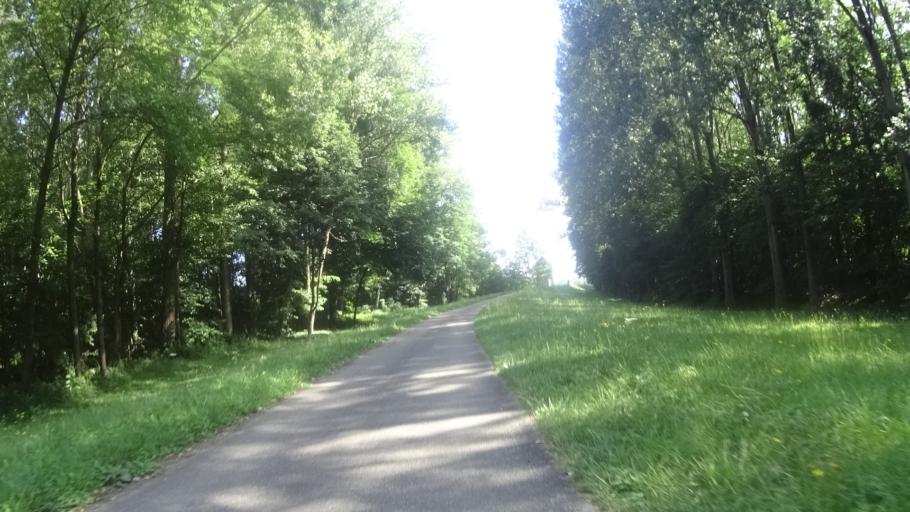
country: DE
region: Rheinland-Pfalz
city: Neupotz
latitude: 49.0808
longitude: 8.3273
